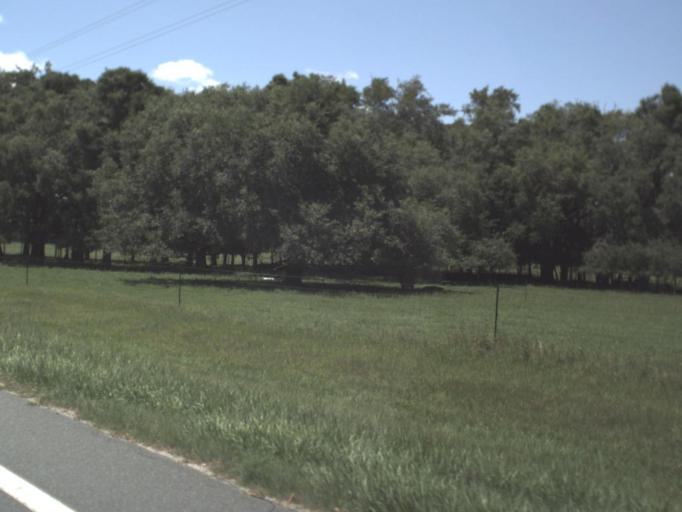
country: US
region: Florida
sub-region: Lafayette County
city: Mayo
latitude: 30.1224
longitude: -83.2667
